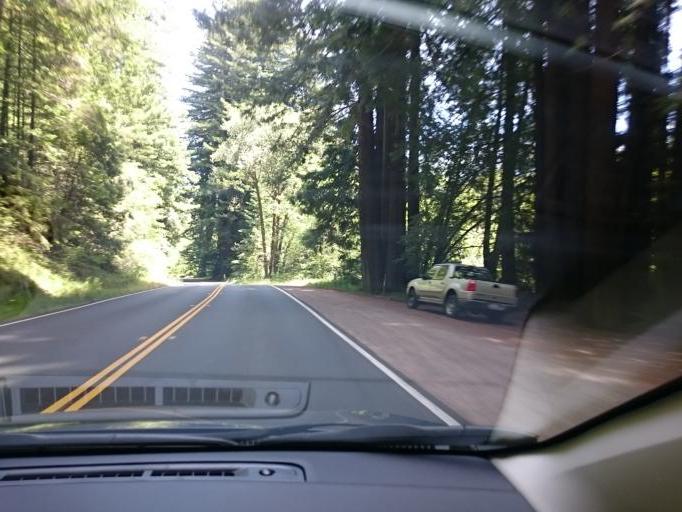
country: US
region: California
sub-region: Mendocino County
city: Fort Bragg
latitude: 39.1777
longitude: -123.6875
